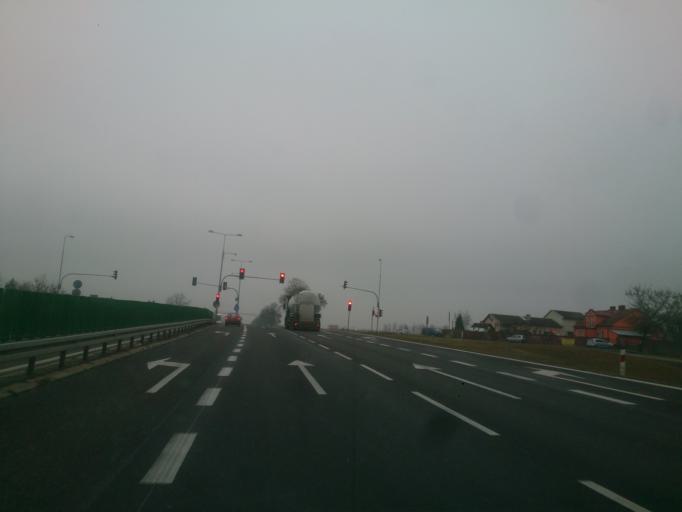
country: PL
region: Masovian Voivodeship
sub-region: Powiat plonski
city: Zaluski
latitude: 52.5500
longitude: 20.5003
